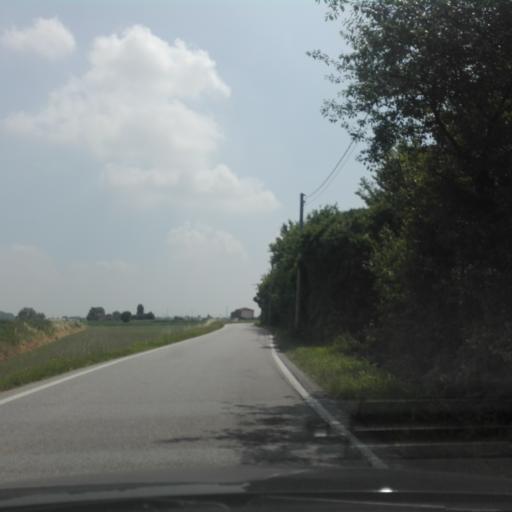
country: IT
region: Veneto
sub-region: Provincia di Rovigo
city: Gavello
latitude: 45.0263
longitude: 11.9190
